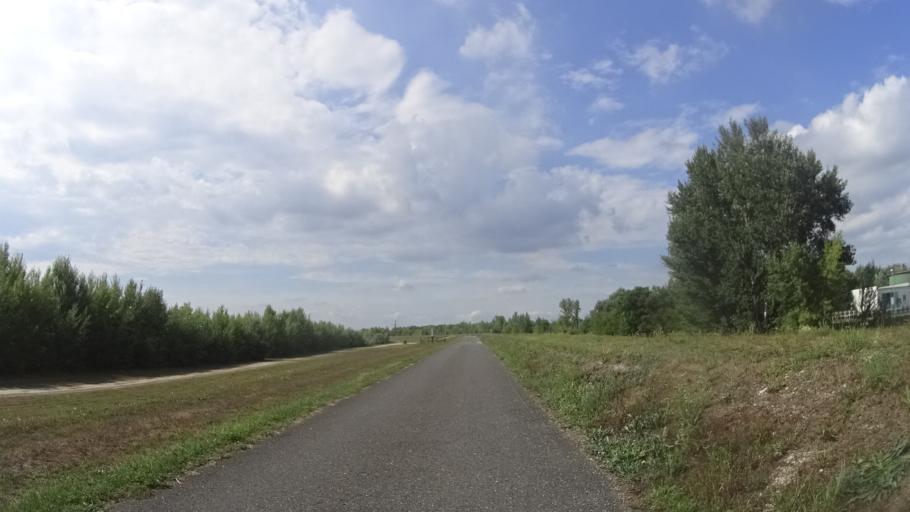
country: SK
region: Trnavsky
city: Gabcikovo
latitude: 47.8727
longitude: 17.5543
